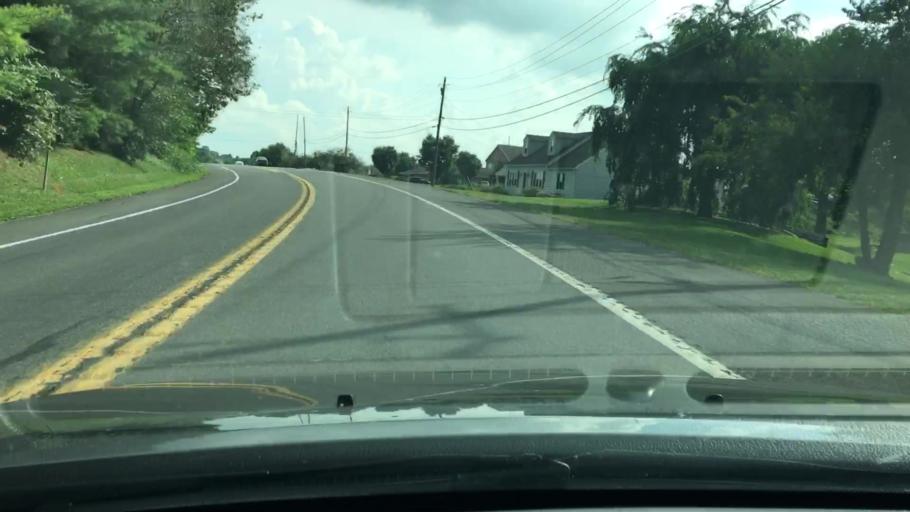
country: US
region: Pennsylvania
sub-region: Franklin County
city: Guilford
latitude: 39.9364
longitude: -77.5906
